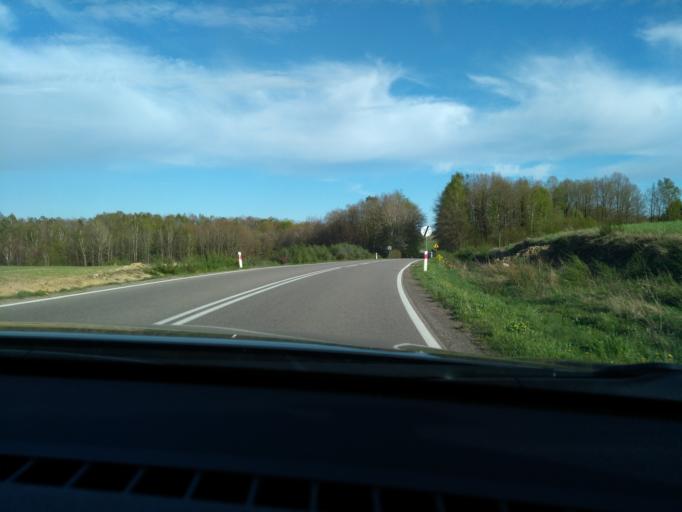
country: PL
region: Pomeranian Voivodeship
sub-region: Powiat leborski
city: Cewice
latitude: 54.3377
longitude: 17.7054
